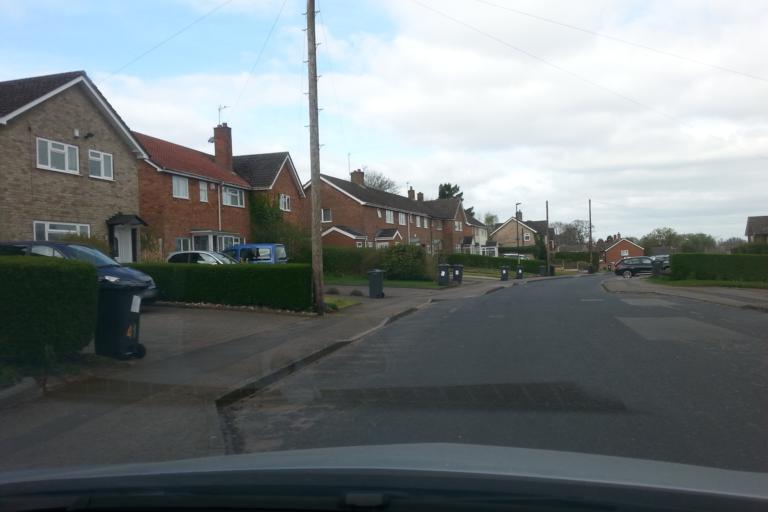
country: GB
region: England
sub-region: Walsall
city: Streetly
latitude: 52.5965
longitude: -1.8475
